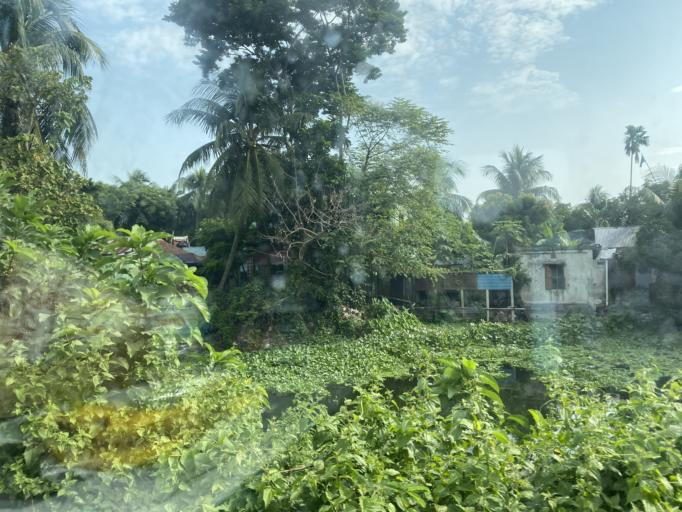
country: BD
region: Chittagong
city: Nabinagar
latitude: 23.9526
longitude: 91.1198
